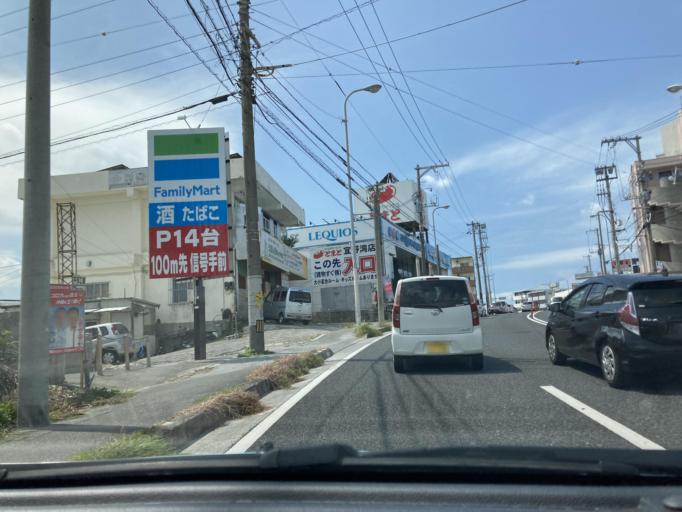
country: JP
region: Okinawa
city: Ginowan
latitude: 26.2580
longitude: 127.7573
